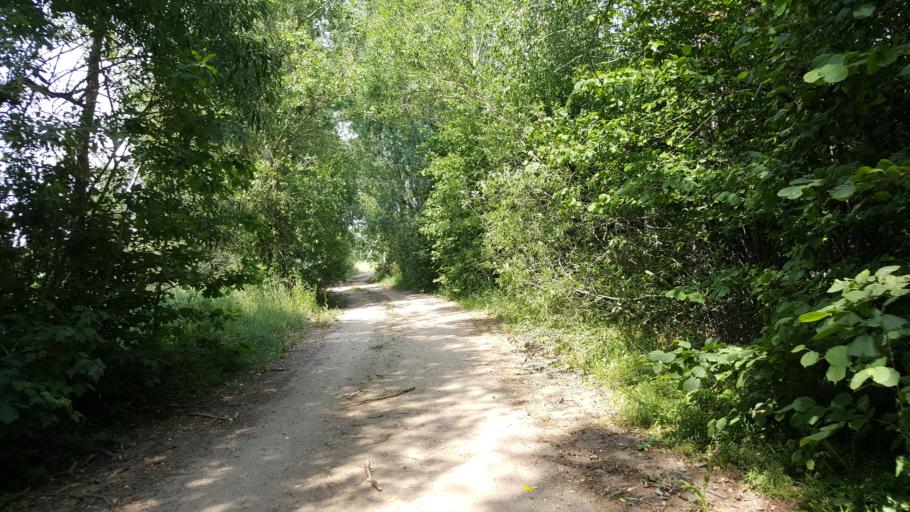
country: BY
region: Brest
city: Kamyanyets
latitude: 52.3626
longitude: 23.7620
